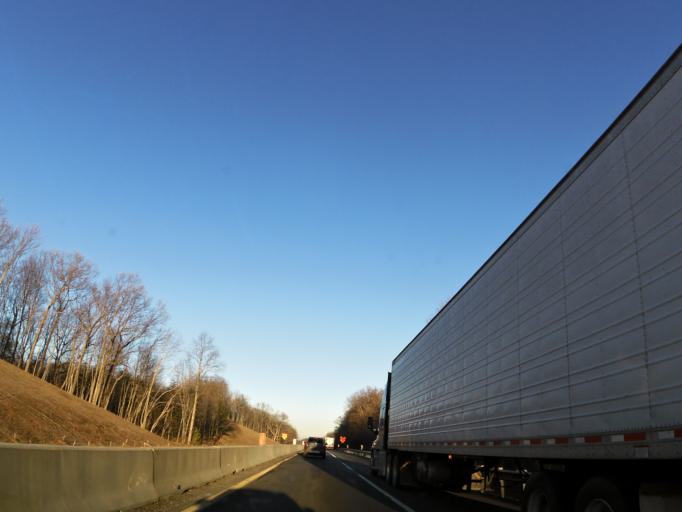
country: US
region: Tennessee
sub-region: Campbell County
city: Jacksboro
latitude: 36.4446
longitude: -84.2763
